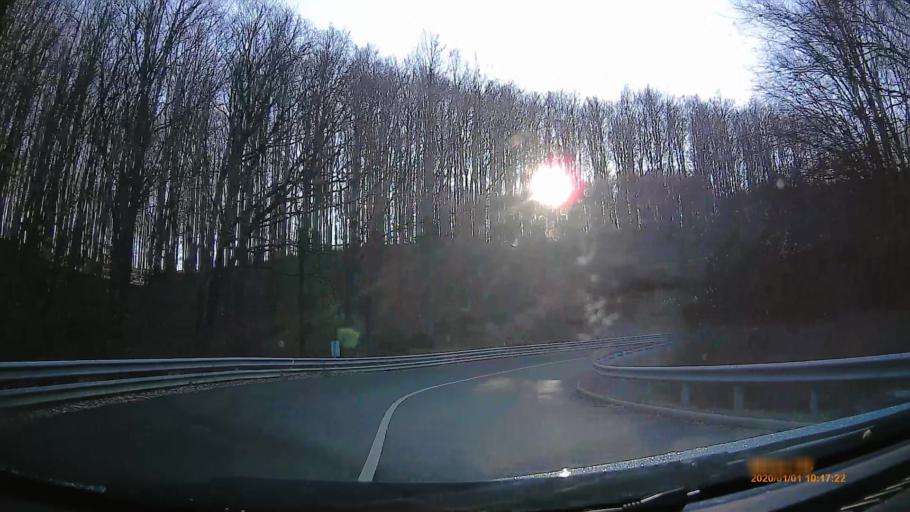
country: HU
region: Heves
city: Paradsasvar
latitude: 47.9092
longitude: 19.9902
